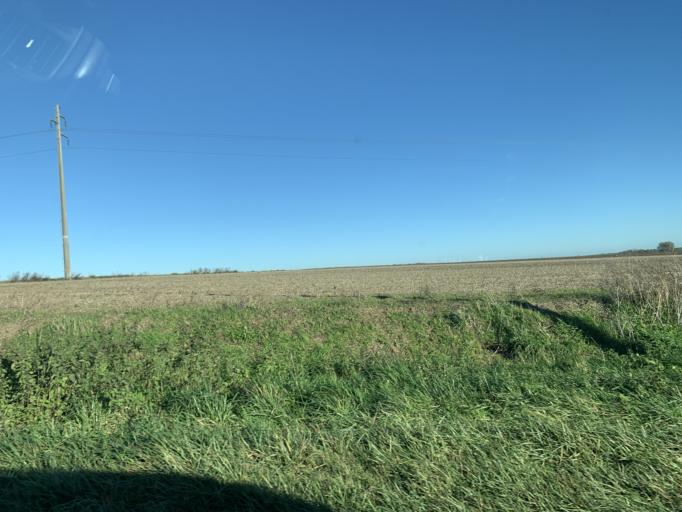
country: FR
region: Nord-Pas-de-Calais
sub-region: Departement du Nord
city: Escaudoeuvres
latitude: 50.1596
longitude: 3.3008
